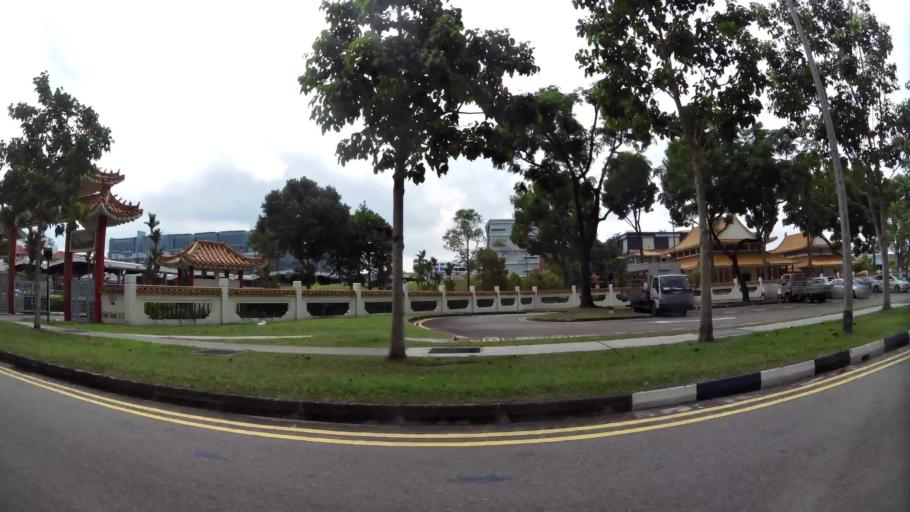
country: SG
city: Singapore
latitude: 1.3416
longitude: 103.7539
